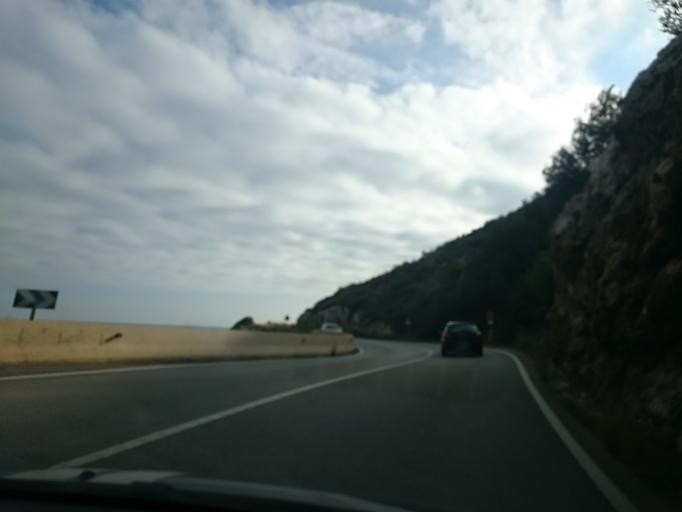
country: ES
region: Catalonia
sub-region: Provincia de Barcelona
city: Sitges
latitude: 41.2428
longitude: 1.8674
